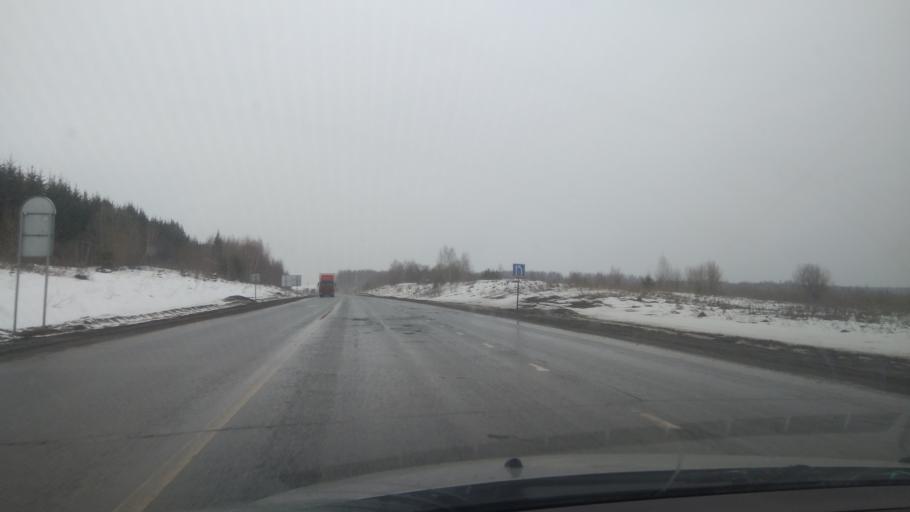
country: RU
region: Perm
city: Kungur
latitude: 57.3866
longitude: 56.9045
